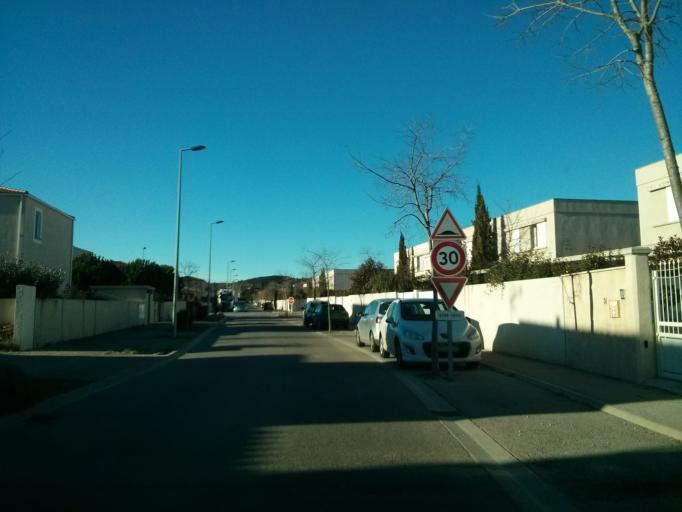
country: FR
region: Languedoc-Roussillon
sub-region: Departement du Gard
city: Calvisson
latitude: 43.7848
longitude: 4.2009
